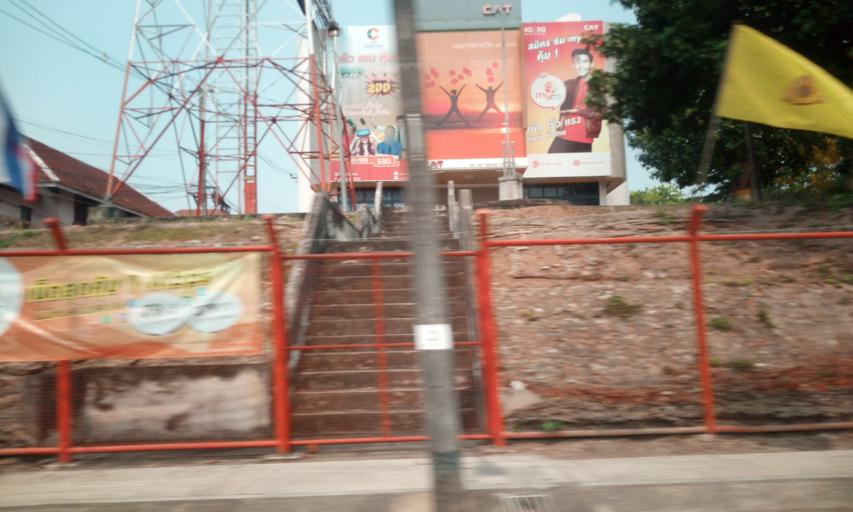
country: TH
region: Chiang Rai
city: Chiang Rai
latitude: 19.9108
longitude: 99.8263
